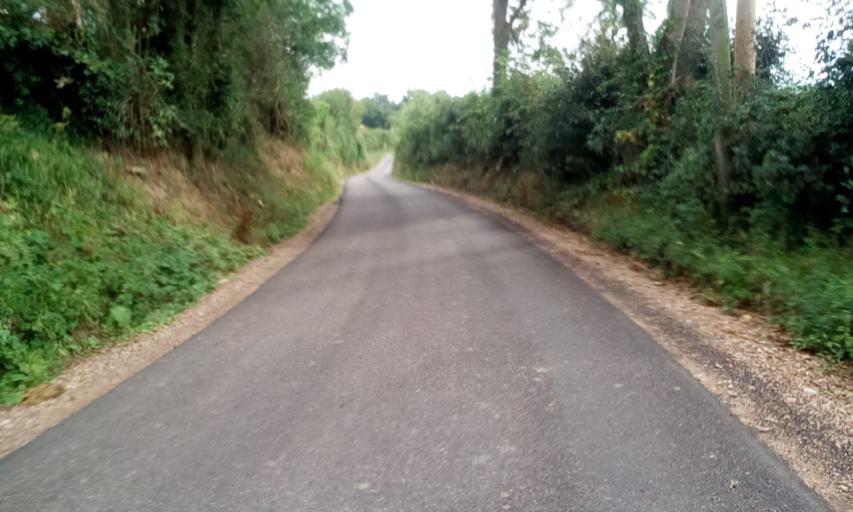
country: FR
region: Lower Normandy
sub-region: Departement du Calvados
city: Troarn
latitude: 49.1977
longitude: -0.1524
